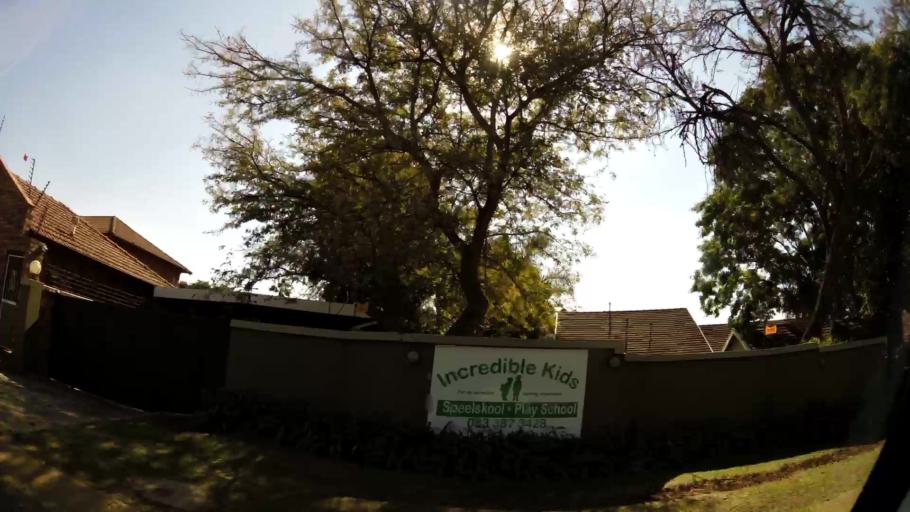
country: ZA
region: Gauteng
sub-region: City of Tshwane Metropolitan Municipality
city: Pretoria
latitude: -25.7680
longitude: 28.2711
